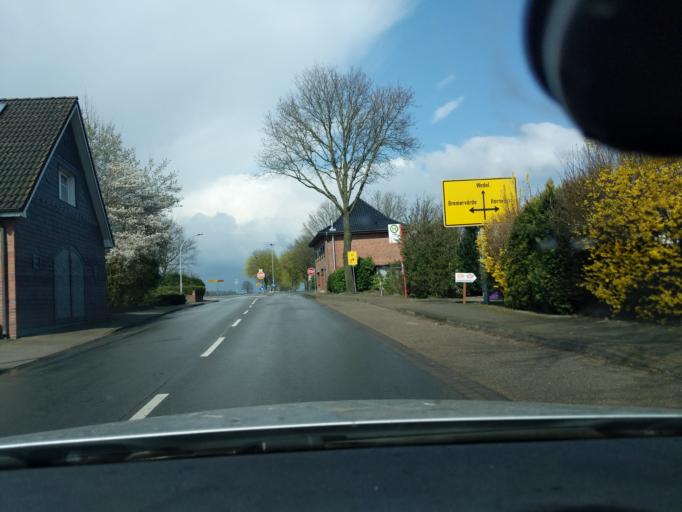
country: DE
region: Lower Saxony
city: Bargstedt
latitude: 53.4606
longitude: 9.4461
